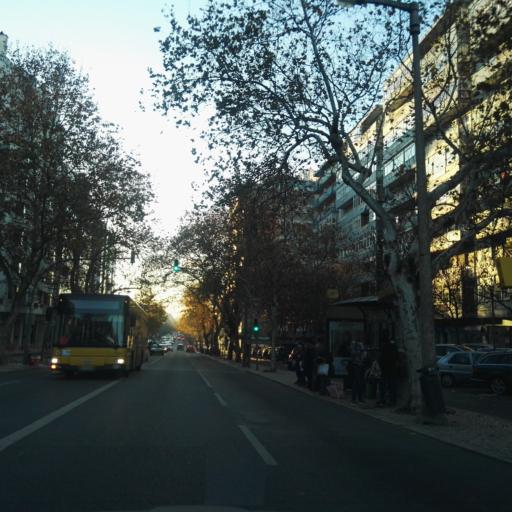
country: PT
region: Lisbon
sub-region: Loures
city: Moscavide
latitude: 38.7596
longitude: -9.1370
